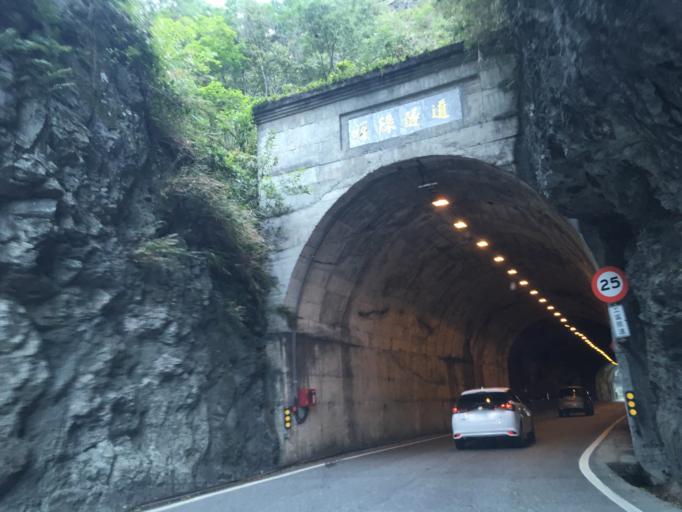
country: TW
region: Taiwan
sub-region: Hualien
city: Hualian
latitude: 24.1767
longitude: 121.5017
